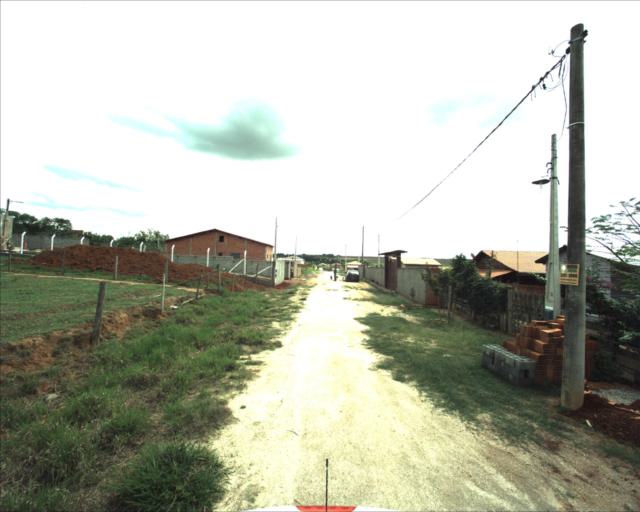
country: BR
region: Sao Paulo
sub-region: Aracoiaba Da Serra
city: Aracoiaba da Serra
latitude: -23.5478
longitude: -47.5464
